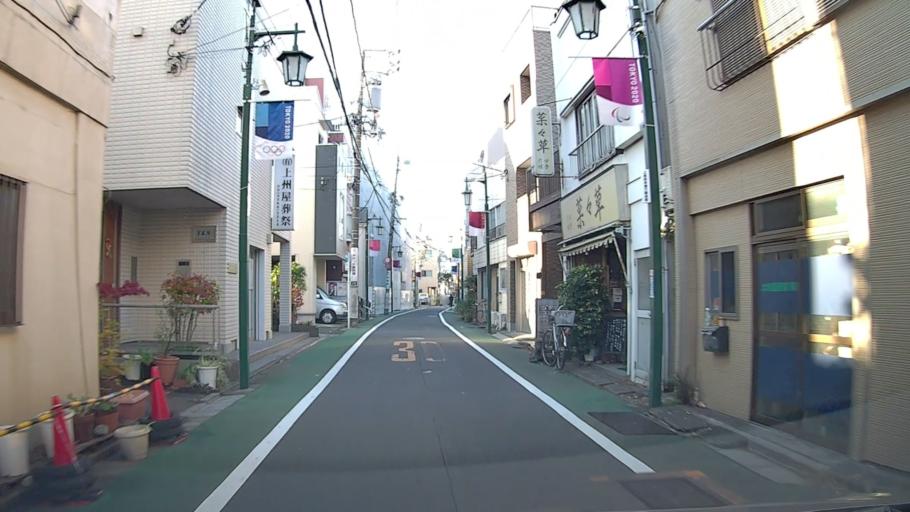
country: JP
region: Tokyo
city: Tokyo
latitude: 35.7136
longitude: 139.6723
